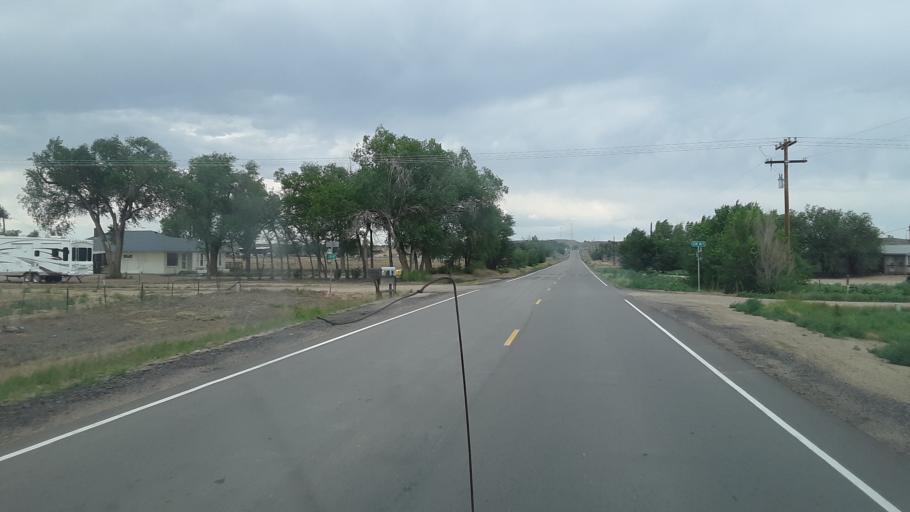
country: US
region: Colorado
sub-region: Otero County
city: Fowler
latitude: 38.1481
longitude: -104.0231
